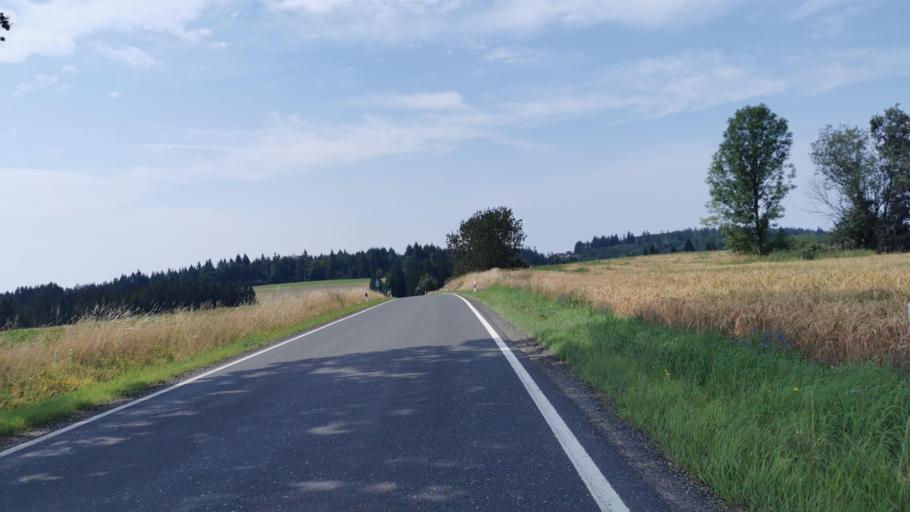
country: DE
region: Bavaria
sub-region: Upper Franconia
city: Wilhelmsthal
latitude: 50.3110
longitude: 11.4034
